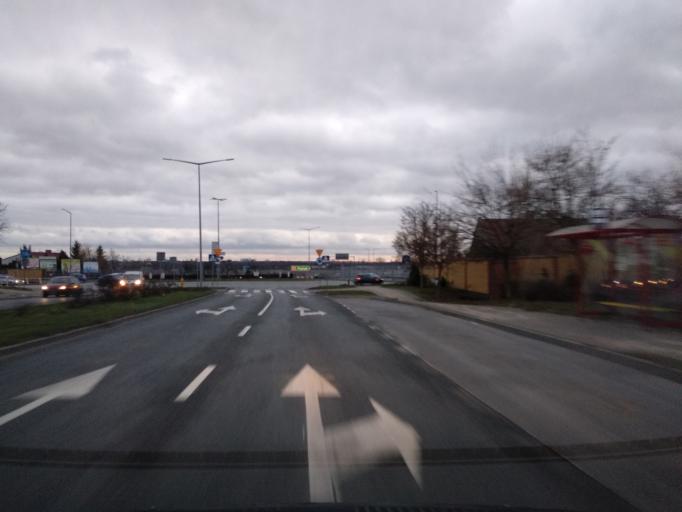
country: PL
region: Greater Poland Voivodeship
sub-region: Konin
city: Konin
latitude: 52.2269
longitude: 18.2442
